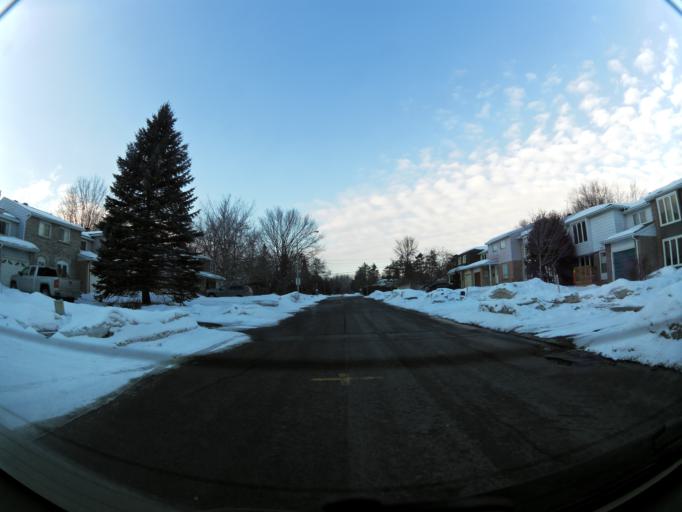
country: CA
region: Ontario
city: Ottawa
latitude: 45.4352
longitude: -75.5538
